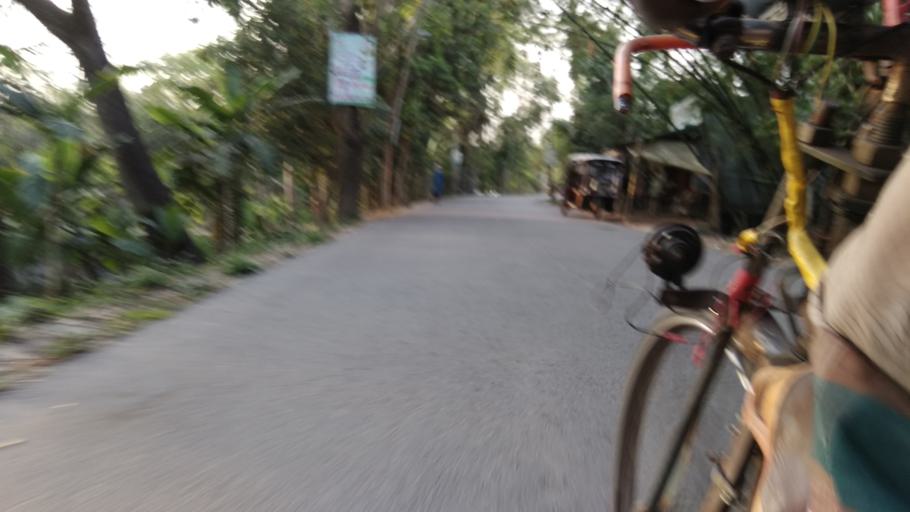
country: BD
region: Barisal
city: Mehendiganj
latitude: 22.9231
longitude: 90.4062
